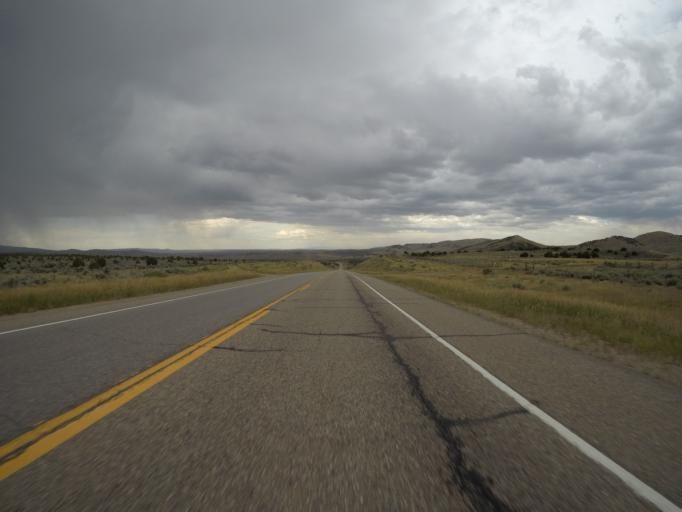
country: US
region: Colorado
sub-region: Rio Blanco County
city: Rangely
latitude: 40.3756
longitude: -108.3739
